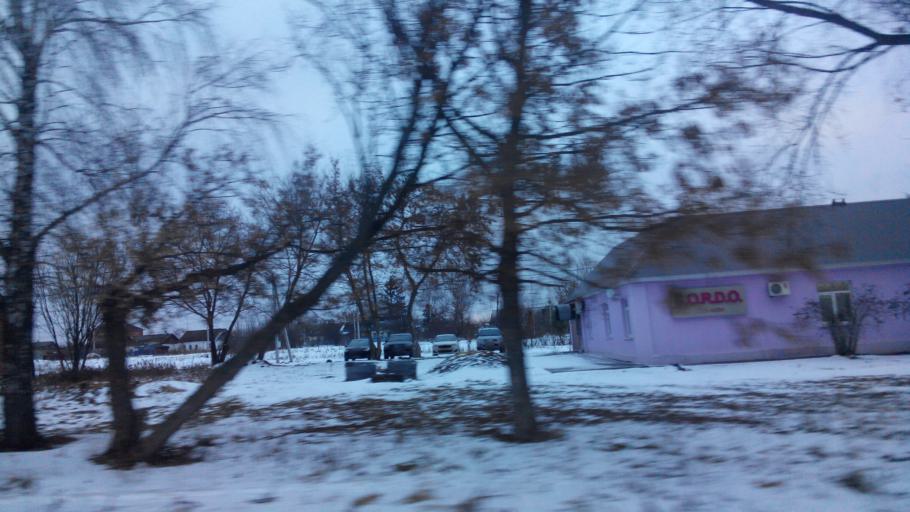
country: RU
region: Tula
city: Mayskiy
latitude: 53.9781
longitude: 38.2325
